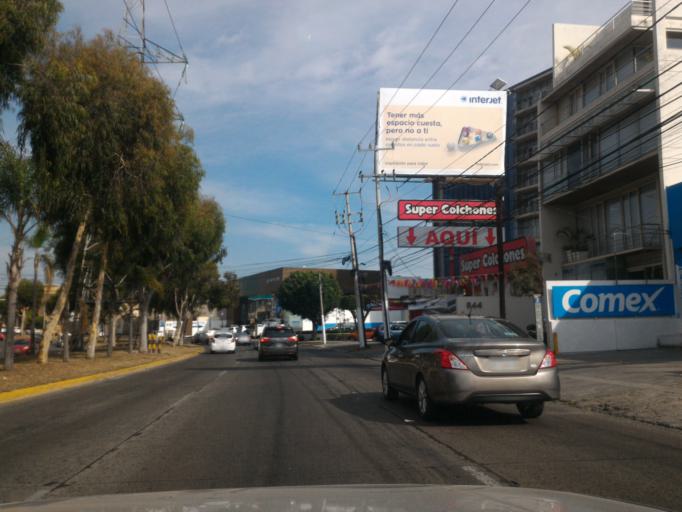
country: MX
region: Jalisco
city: Zapopan2
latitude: 20.6900
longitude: -103.4165
